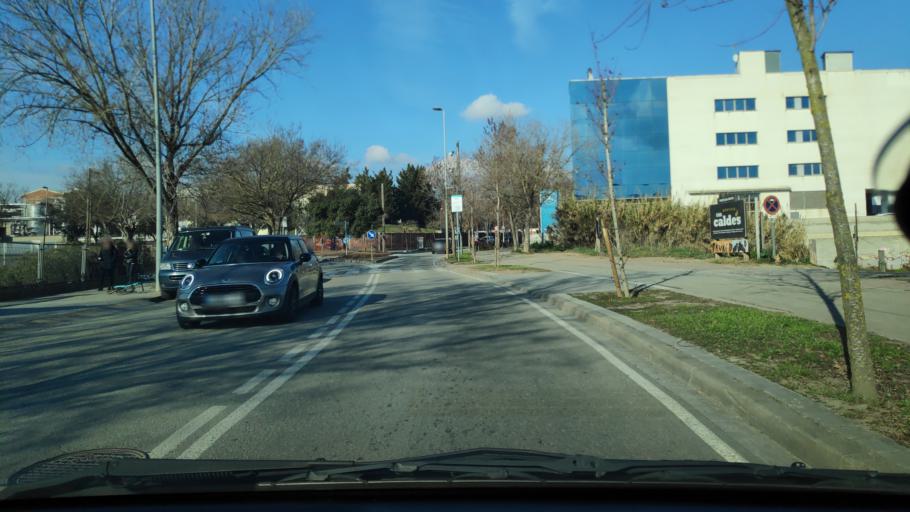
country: ES
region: Catalonia
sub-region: Provincia de Barcelona
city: Sant Cugat del Valles
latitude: 41.4732
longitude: 2.0976
